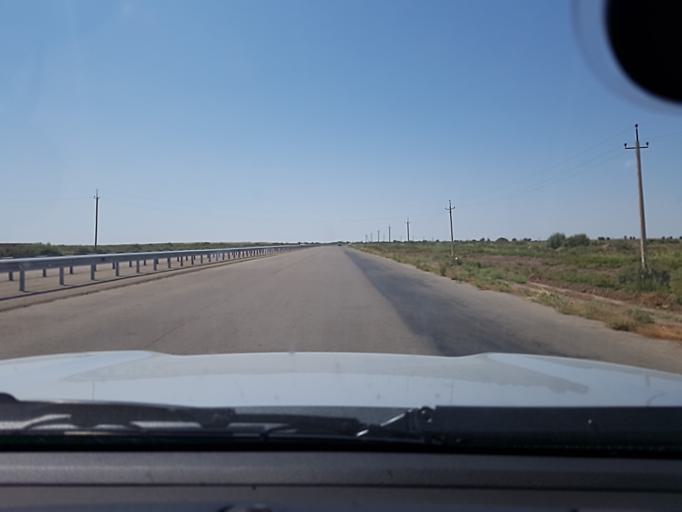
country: TM
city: Akdepe
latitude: 41.7435
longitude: 59.2511
